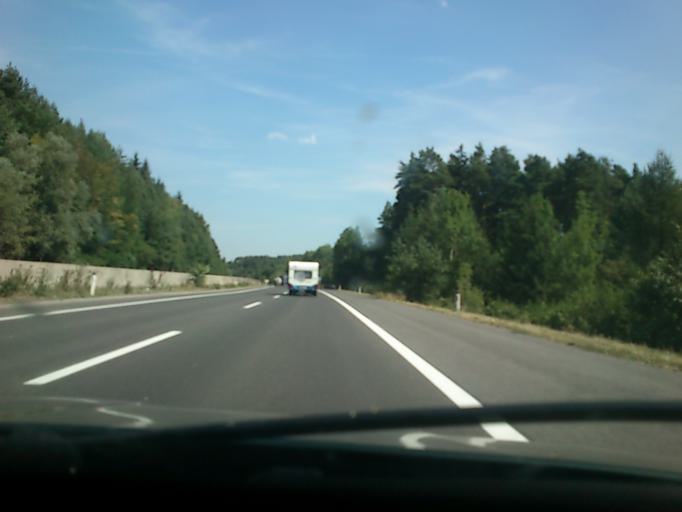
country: AT
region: Lower Austria
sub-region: Politischer Bezirk Neunkirchen
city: Seebenstein
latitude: 47.6915
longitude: 16.1290
